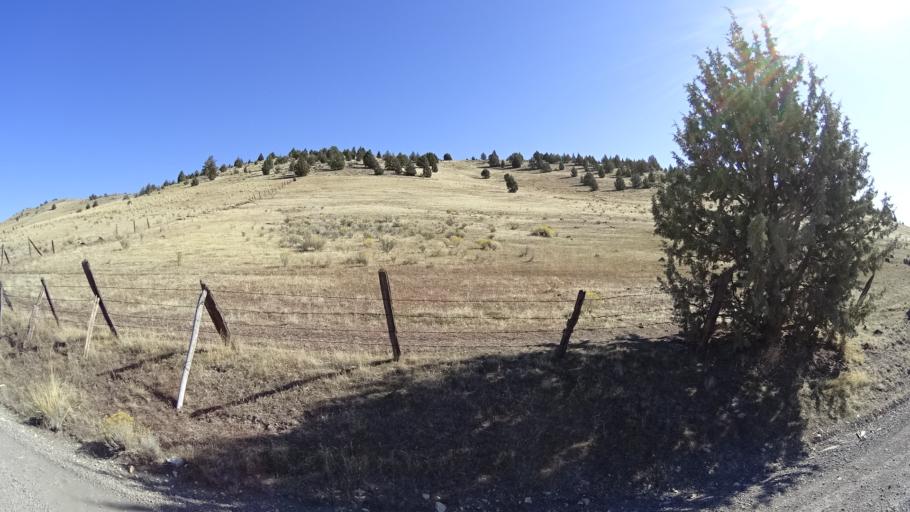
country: US
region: California
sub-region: Siskiyou County
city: Montague
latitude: 41.7335
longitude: -122.3691
